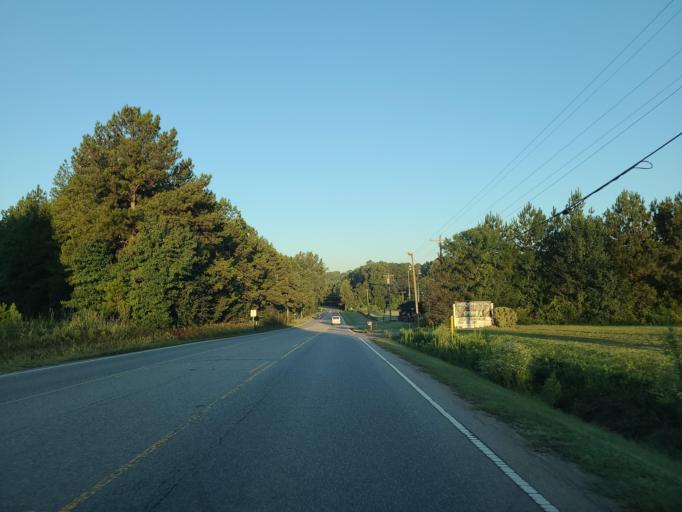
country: US
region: North Carolina
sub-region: Union County
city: Wesley Chapel
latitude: 35.0011
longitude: -80.7124
